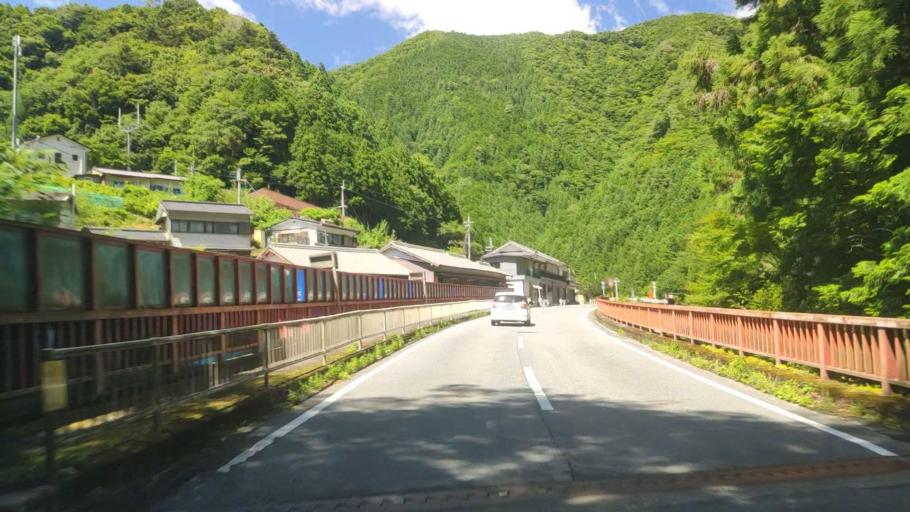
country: JP
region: Mie
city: Owase
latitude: 34.1800
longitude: 136.0049
